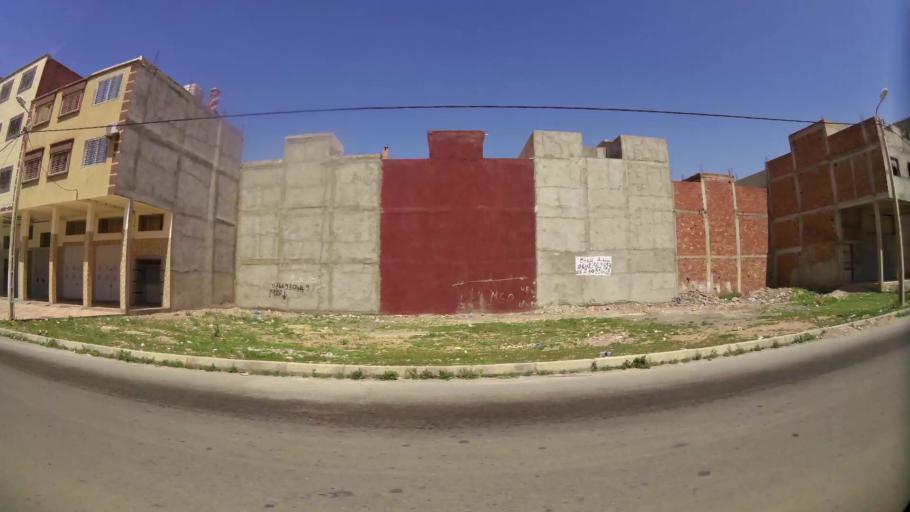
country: MA
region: Oriental
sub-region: Oujda-Angad
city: Oujda
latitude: 34.6992
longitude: -1.8846
